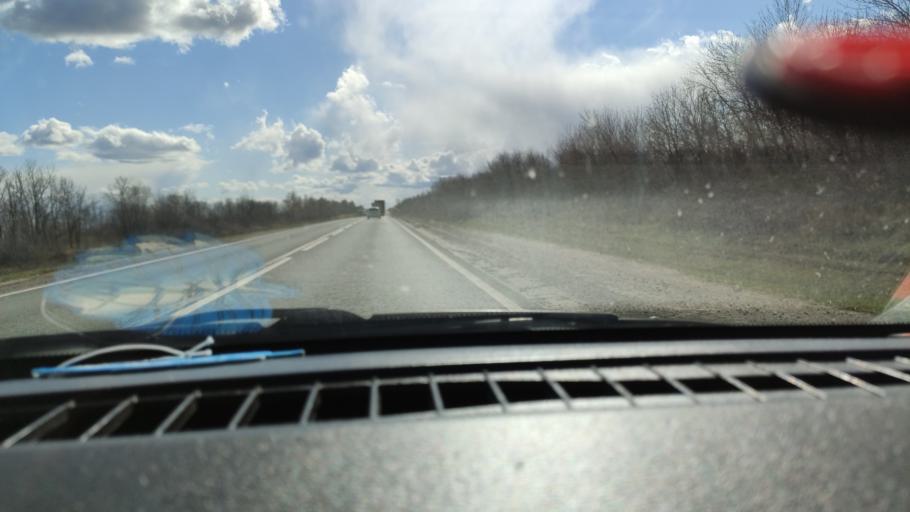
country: RU
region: Saratov
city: Dukhovnitskoye
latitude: 52.6834
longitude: 48.2354
